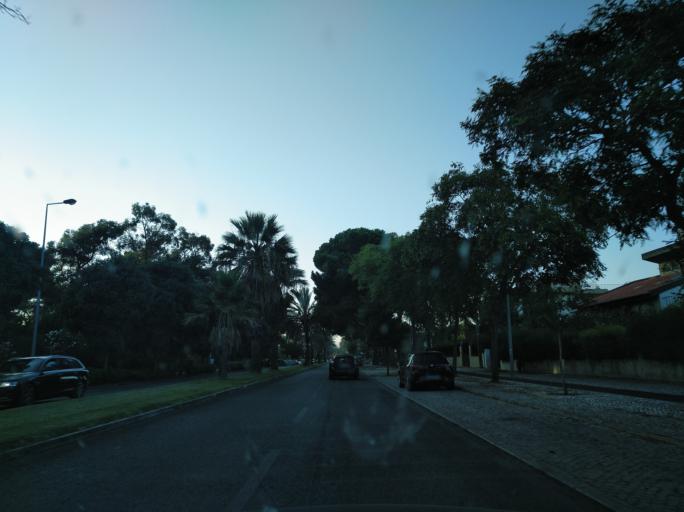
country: PT
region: Setubal
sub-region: Almada
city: Trafaria
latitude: 38.6595
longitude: -9.2412
